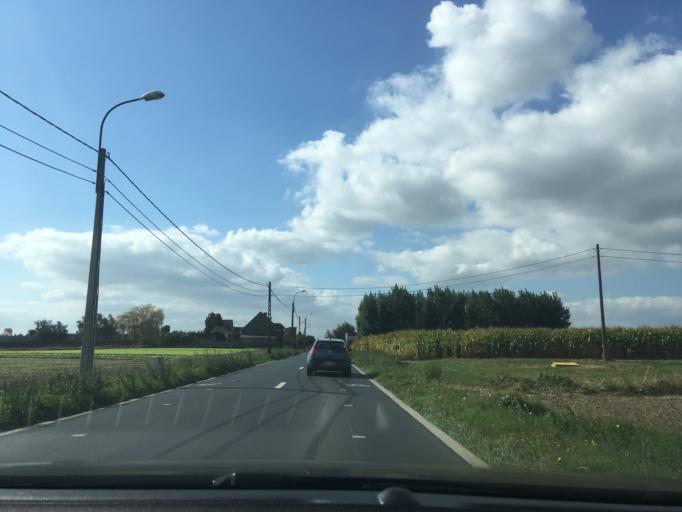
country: BE
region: Flanders
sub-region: Provincie West-Vlaanderen
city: Moorslede
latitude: 50.9176
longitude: 3.0330
